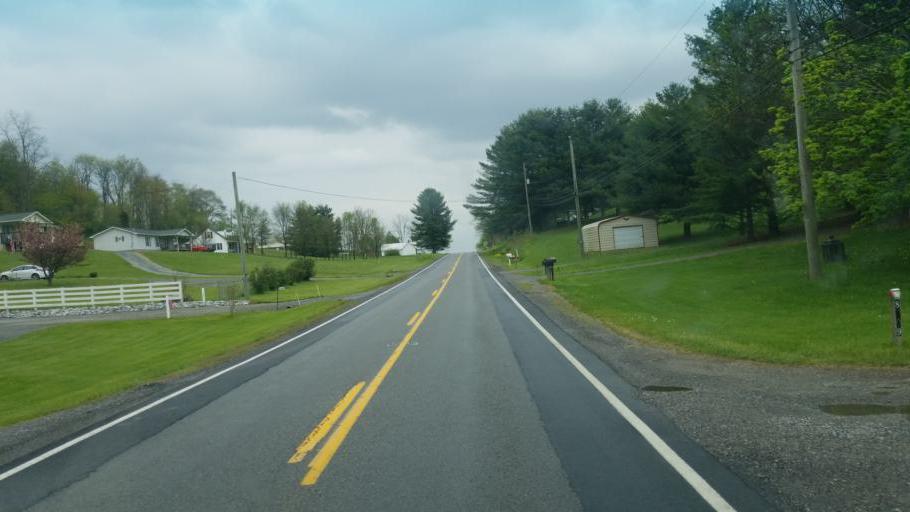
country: US
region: Virginia
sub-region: Wythe County
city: Rural Retreat
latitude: 36.9014
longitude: -81.3181
